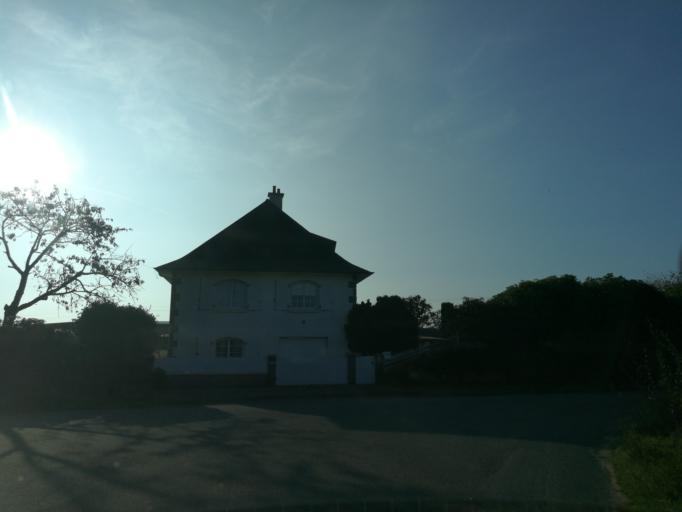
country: FR
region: Brittany
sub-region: Departement d'Ille-et-Vilaine
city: Pleumeleuc
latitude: 48.1726
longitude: -1.9131
